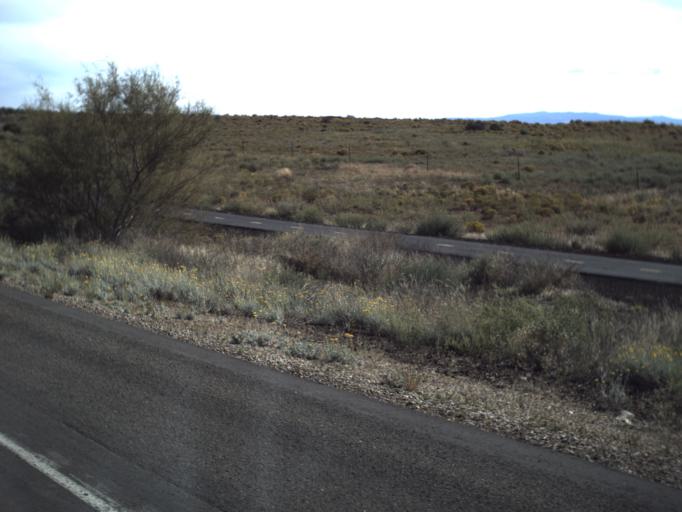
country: US
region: Utah
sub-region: Washington County
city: Ivins
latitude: 37.1931
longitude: -113.6223
